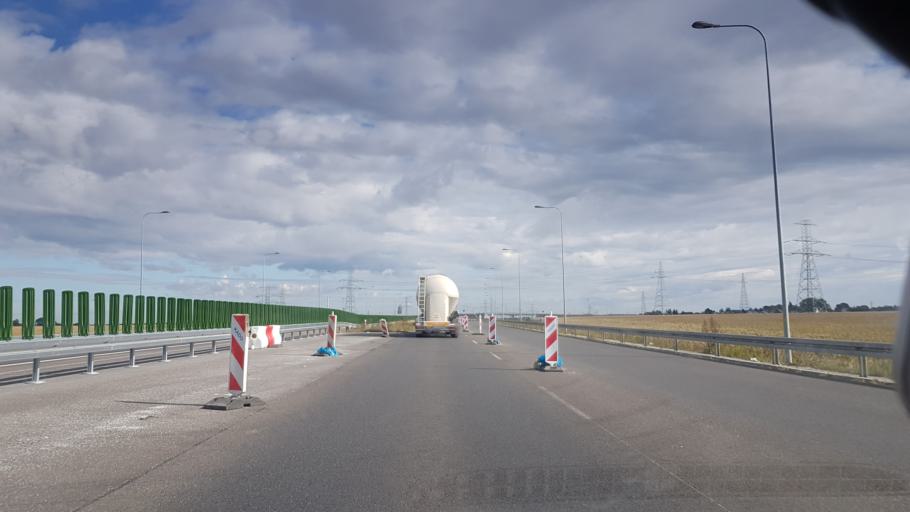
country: PL
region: Greater Poland Voivodeship
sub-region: Powiat poznanski
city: Steszew
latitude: 52.3286
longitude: 16.7250
